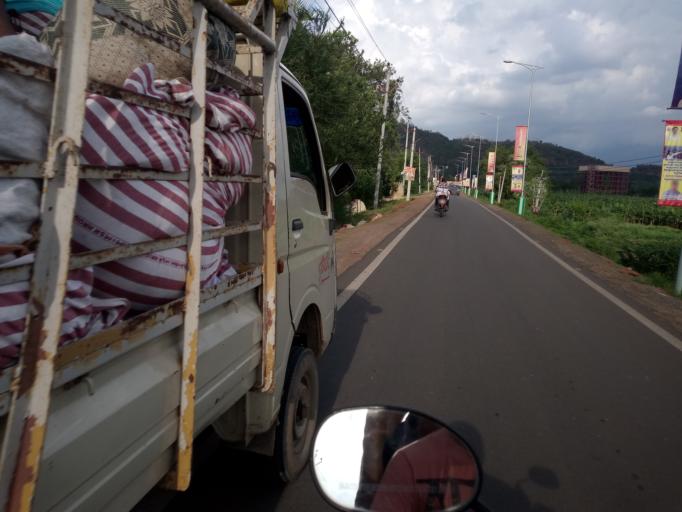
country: IN
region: Andhra Pradesh
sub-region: Guntur
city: Tadepalle
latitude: 16.5005
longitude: 80.5936
